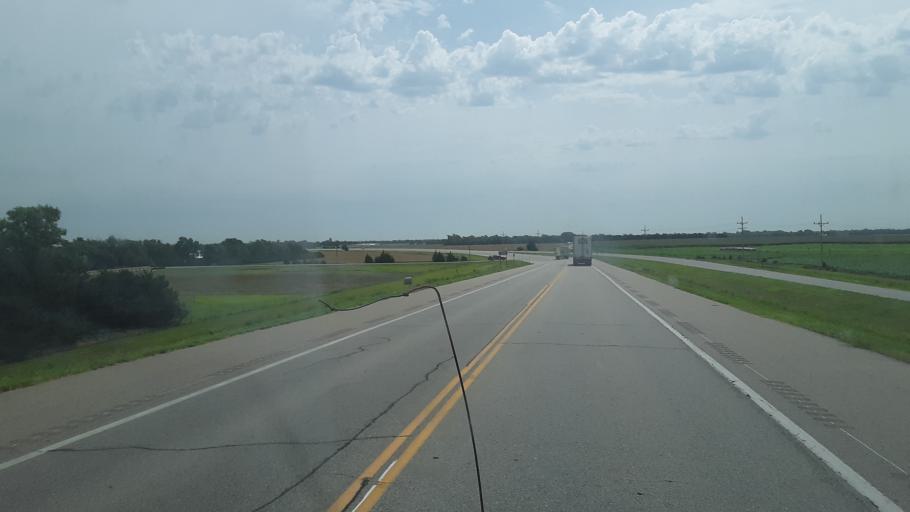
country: US
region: Kansas
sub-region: Reno County
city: South Hutchinson
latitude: 37.9846
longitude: -98.0540
